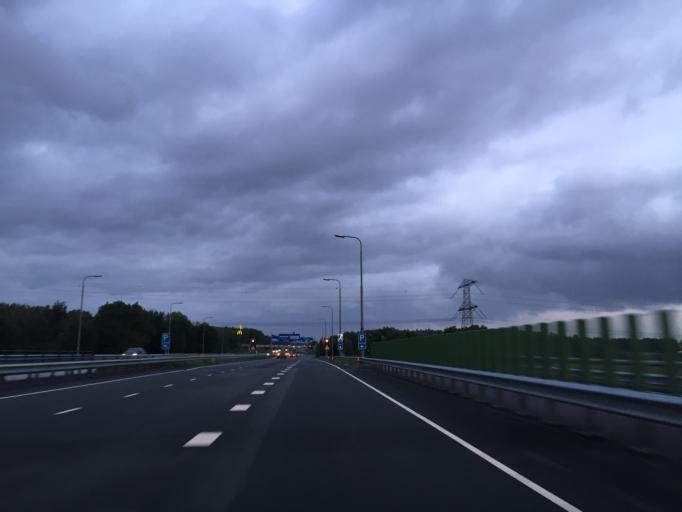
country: NL
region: Flevoland
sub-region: Gemeente Lelystad
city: Lelystad
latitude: 52.4841
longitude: 5.4973
